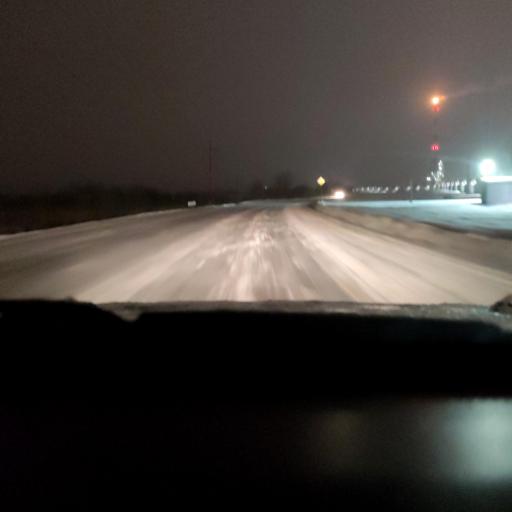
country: RU
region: Perm
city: Gamovo
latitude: 57.9123
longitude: 56.1139
